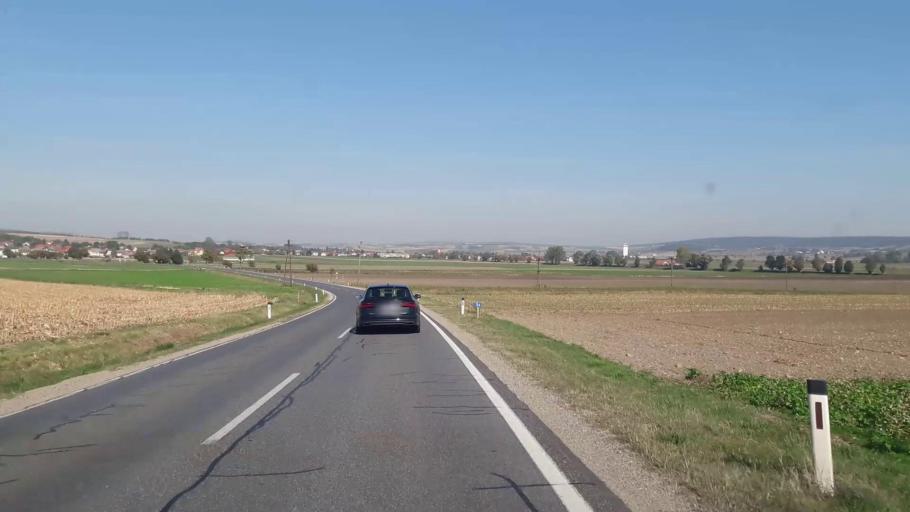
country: AT
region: Lower Austria
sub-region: Politischer Bezirk Korneuburg
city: Harmannsdorf
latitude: 48.3723
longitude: 16.3601
